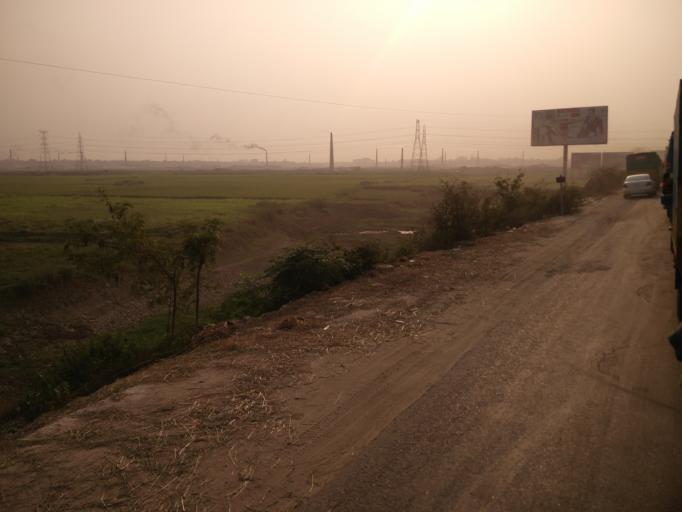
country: BD
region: Dhaka
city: Tungi
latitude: 23.8937
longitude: 90.3532
